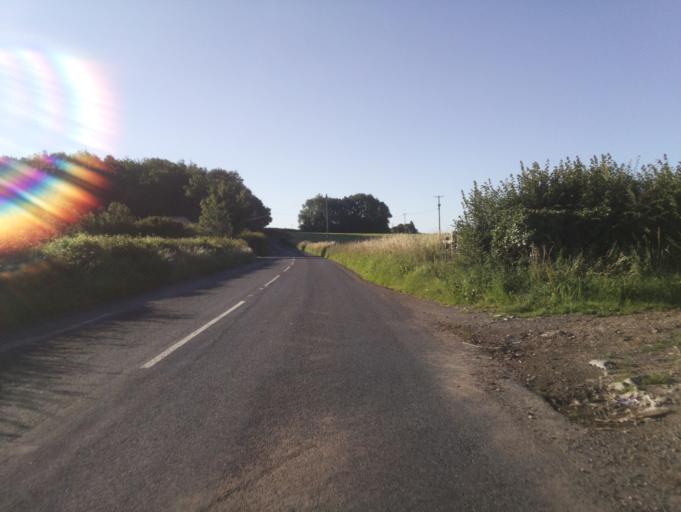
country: GB
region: Wales
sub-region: Monmouthshire
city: Chepstow
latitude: 51.6524
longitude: -2.7159
